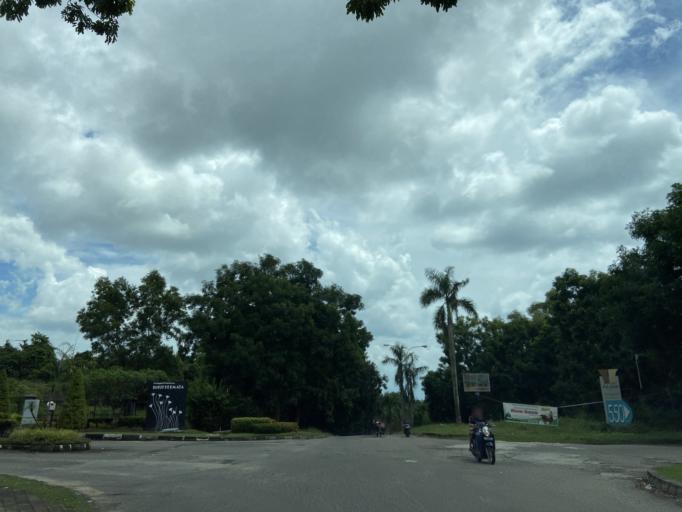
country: SG
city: Singapore
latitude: 1.1309
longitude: 104.0000
